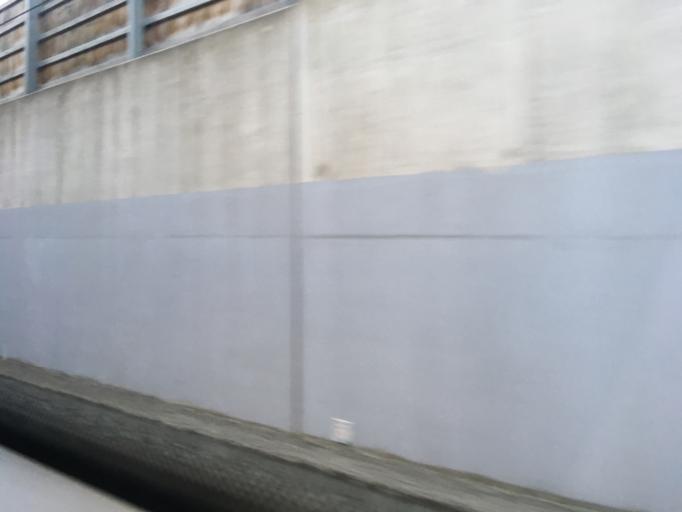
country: GB
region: England
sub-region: Manchester
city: Didsbury
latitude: 53.4174
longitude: -2.2296
